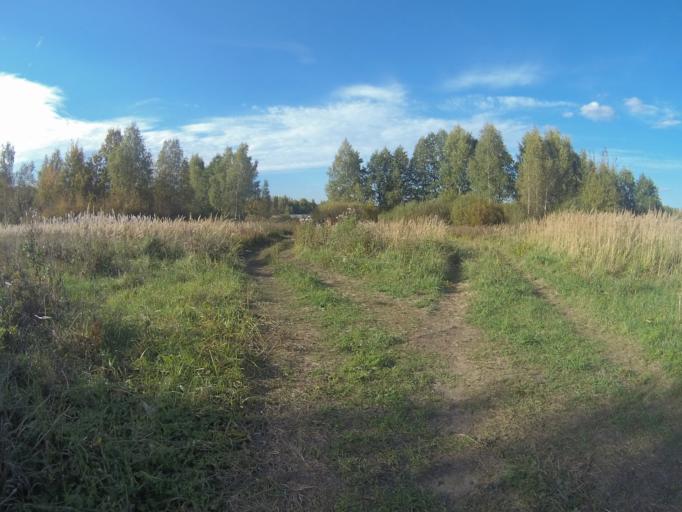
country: RU
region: Vladimir
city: Golovino
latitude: 55.9683
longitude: 40.4541
